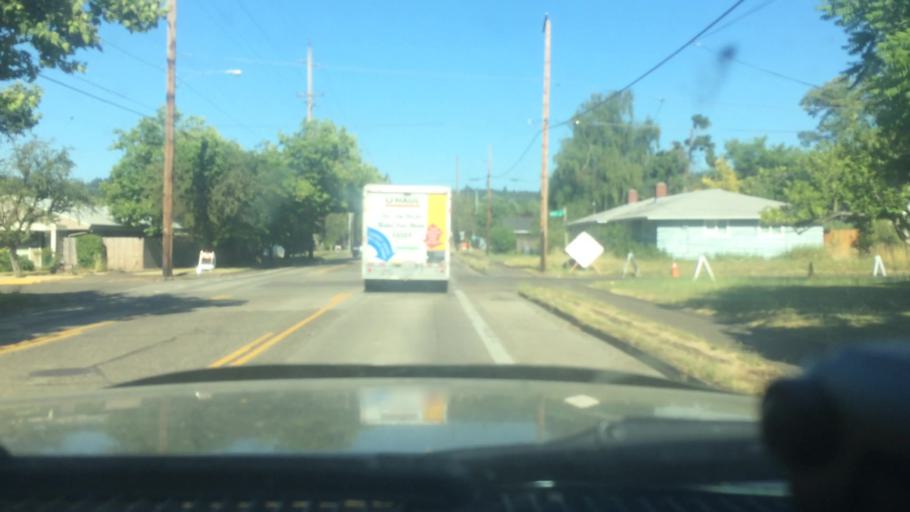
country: US
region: Oregon
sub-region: Lane County
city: Eugene
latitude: 44.0262
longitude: -123.0870
